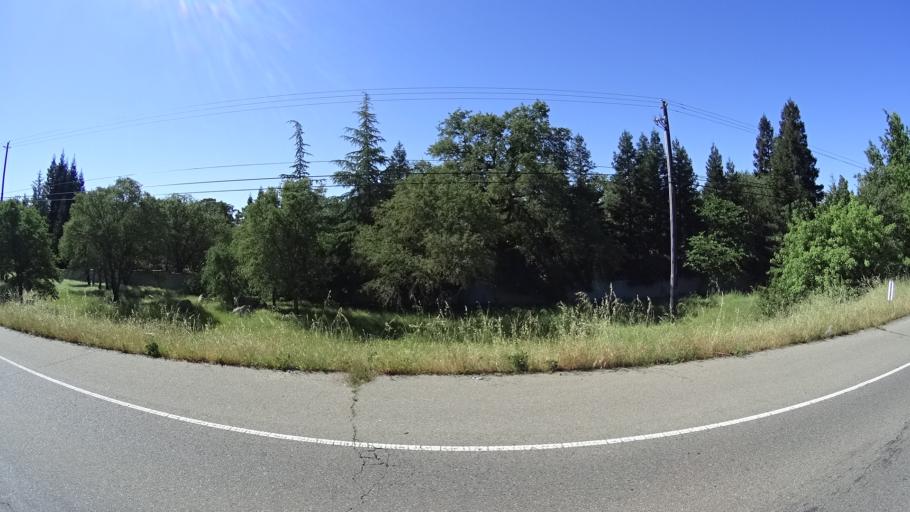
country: US
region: California
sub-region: Placer County
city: Loomis
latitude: 38.7886
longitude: -121.1979
